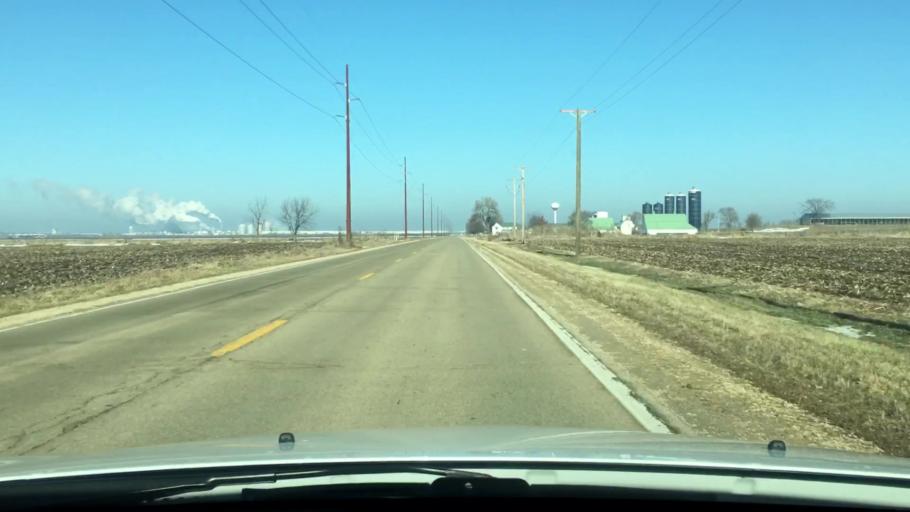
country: US
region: Illinois
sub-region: Ogle County
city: Rochelle
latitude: 41.8661
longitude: -89.0249
